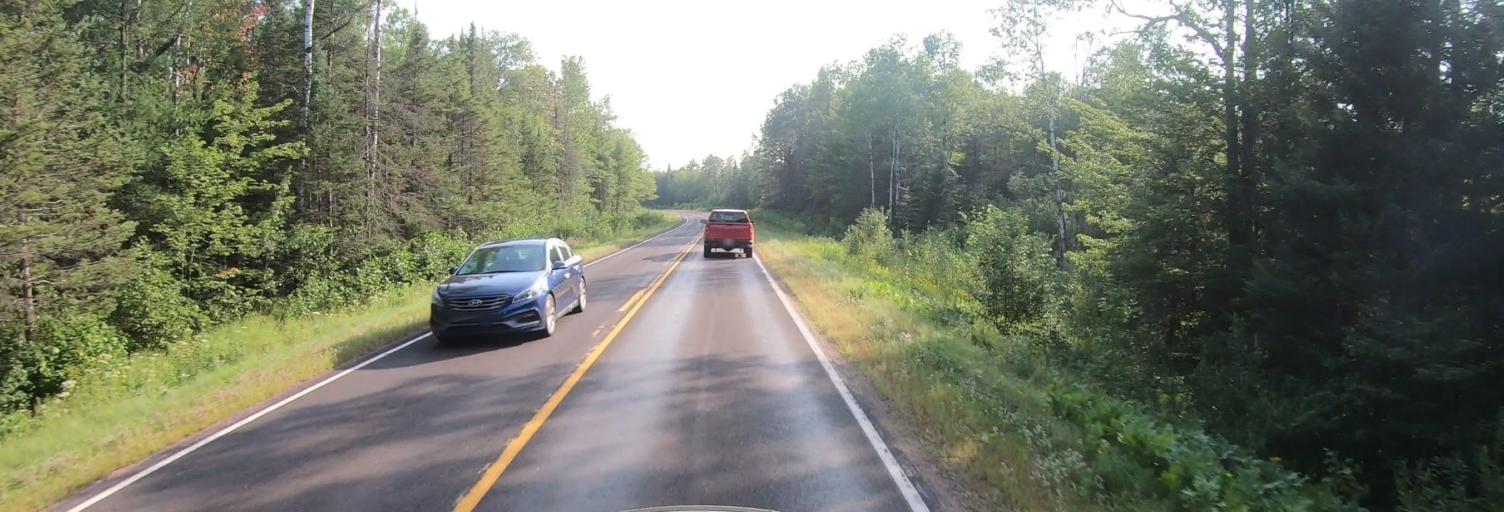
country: US
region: Wisconsin
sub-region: Ashland County
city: Ashland
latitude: 46.2146
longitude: -90.8501
